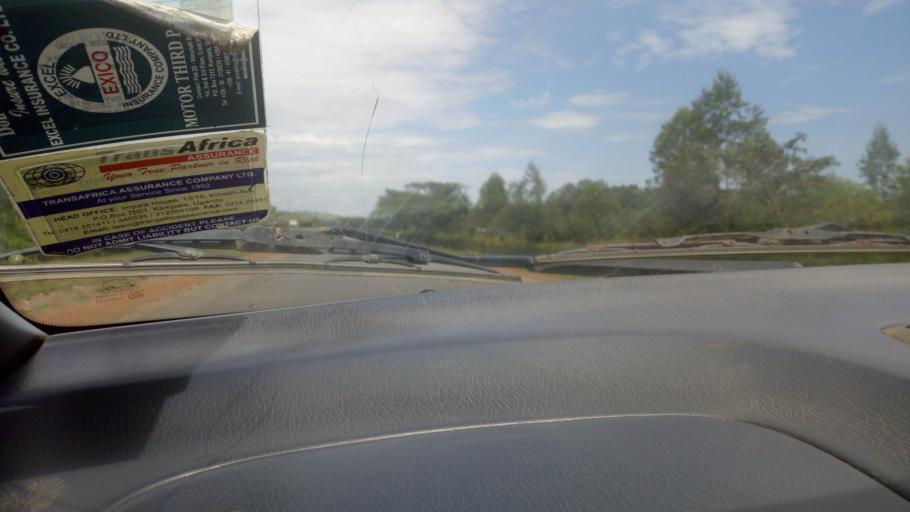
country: UG
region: Western Region
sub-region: Mbarara District
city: Bwizibwera
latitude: -0.3843
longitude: 30.5653
